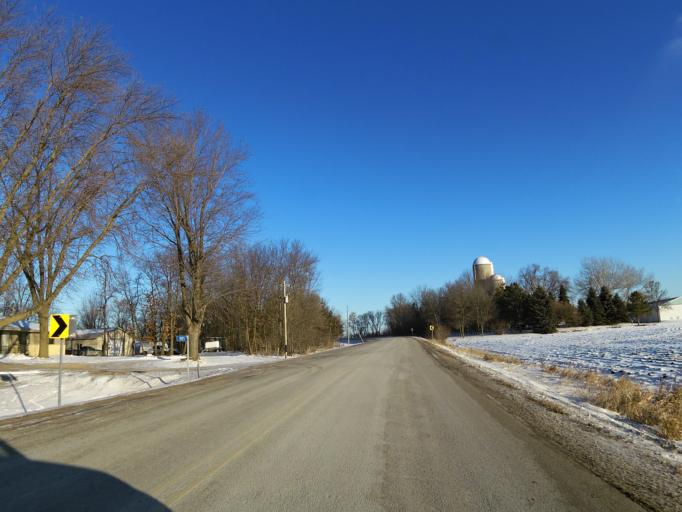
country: US
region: Minnesota
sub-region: Scott County
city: Jordan
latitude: 44.6608
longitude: -93.5316
